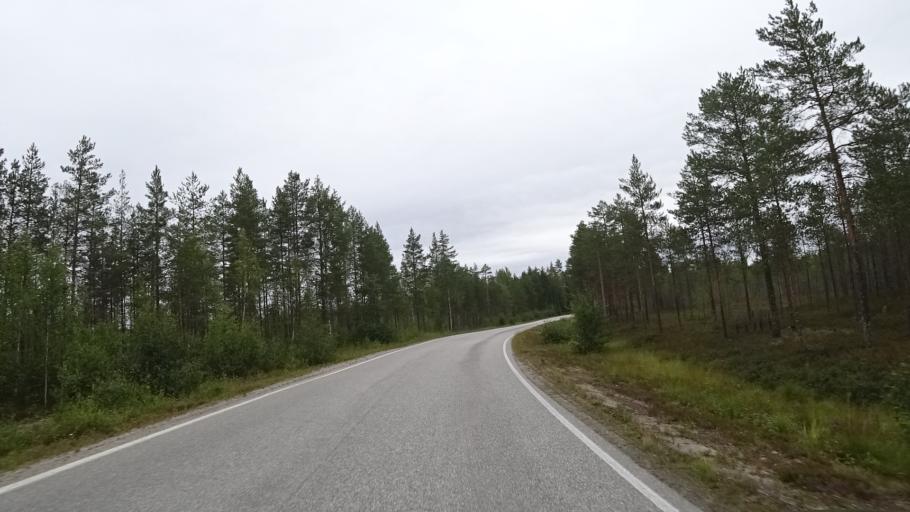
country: FI
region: North Karelia
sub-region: Pielisen Karjala
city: Lieksa
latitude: 63.3581
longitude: 30.2612
